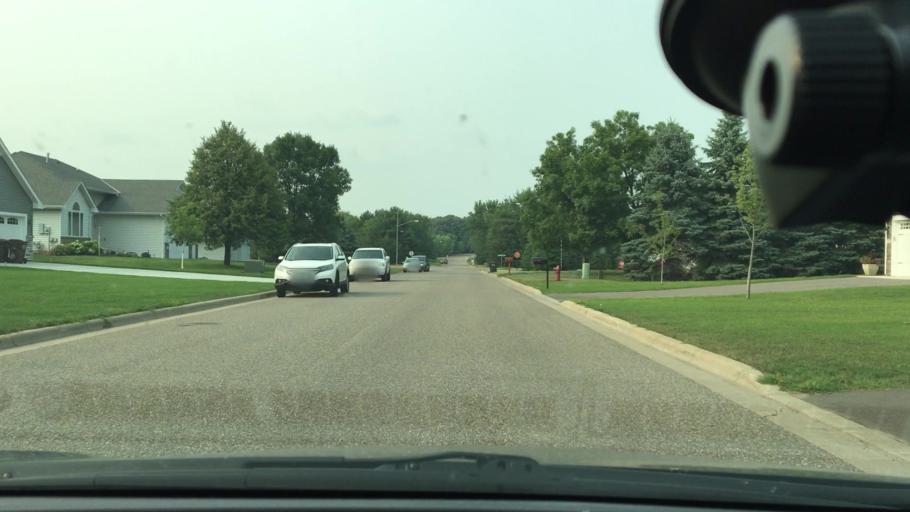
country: US
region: Minnesota
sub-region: Hennepin County
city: Champlin
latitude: 45.1977
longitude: -93.4311
